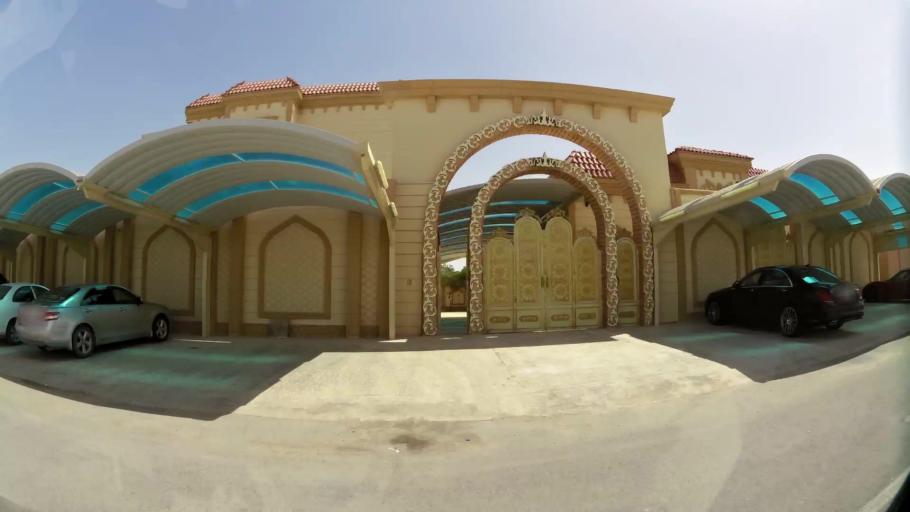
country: QA
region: Baladiyat Umm Salal
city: Umm Salal Muhammad
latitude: 25.3707
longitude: 51.4281
